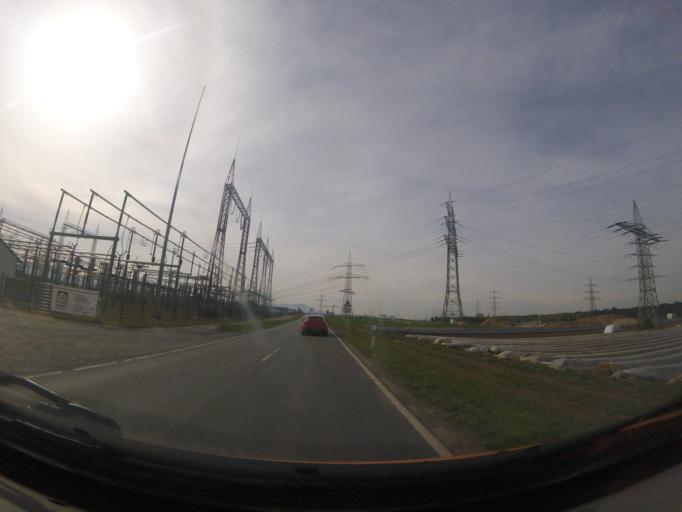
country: DE
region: Hesse
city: Pfungstadt
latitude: 49.8175
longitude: 8.5863
